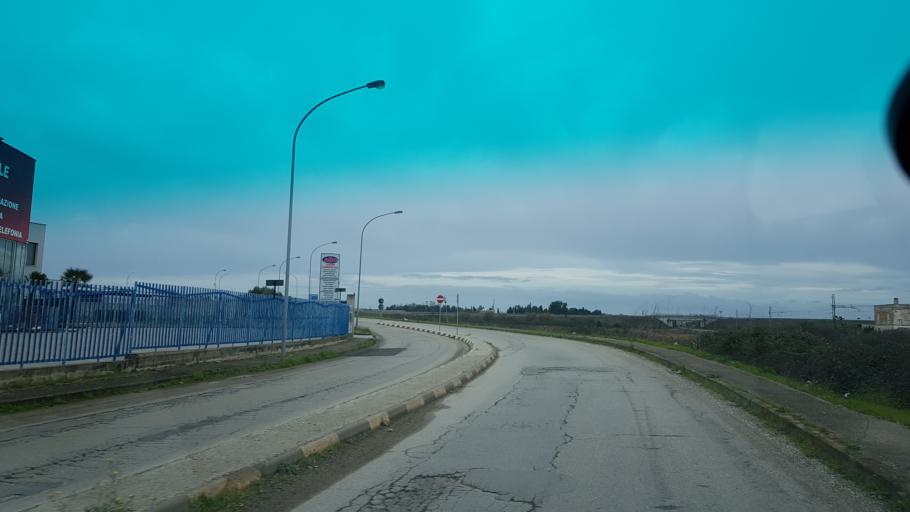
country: IT
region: Apulia
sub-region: Provincia di Brindisi
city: Mesagne
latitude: 40.5729
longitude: 17.8216
